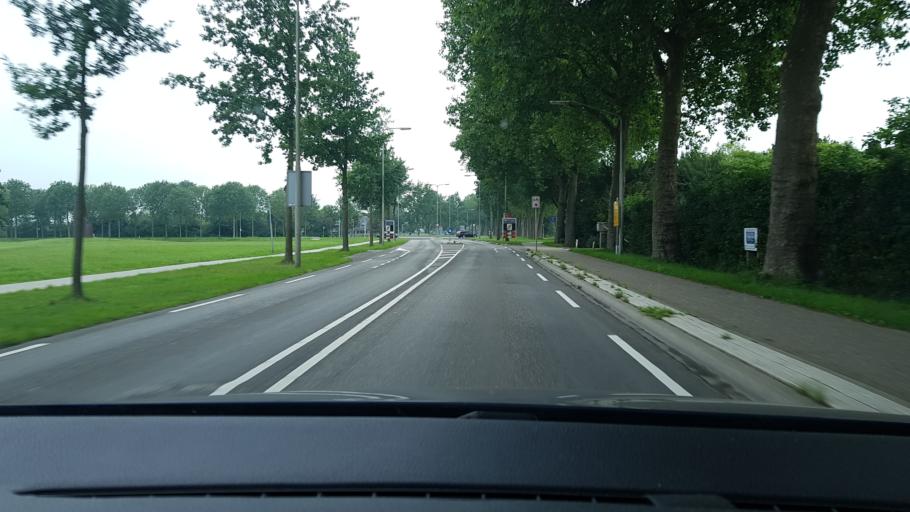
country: NL
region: Gelderland
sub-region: Gemeente Beuningen
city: Beuningen
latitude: 51.8693
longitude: 5.7582
